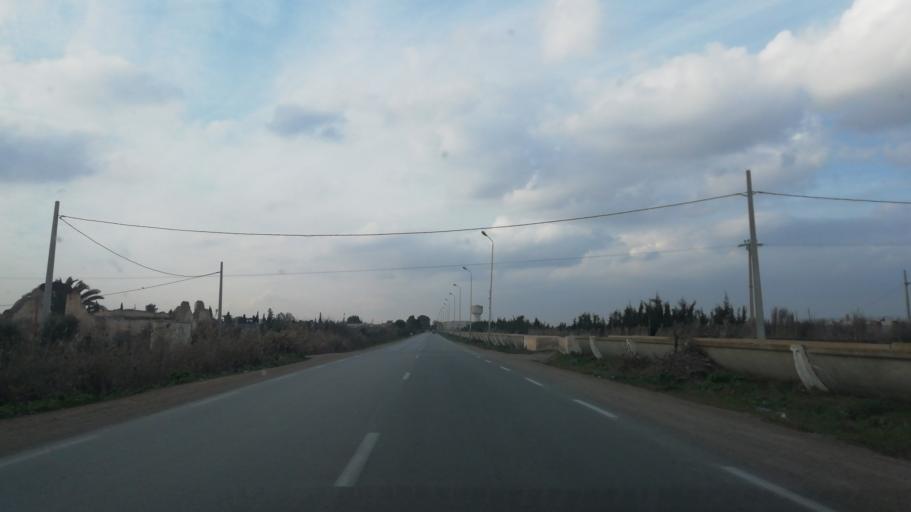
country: DZ
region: Mascara
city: Sig
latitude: 35.6519
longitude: 0.0206
